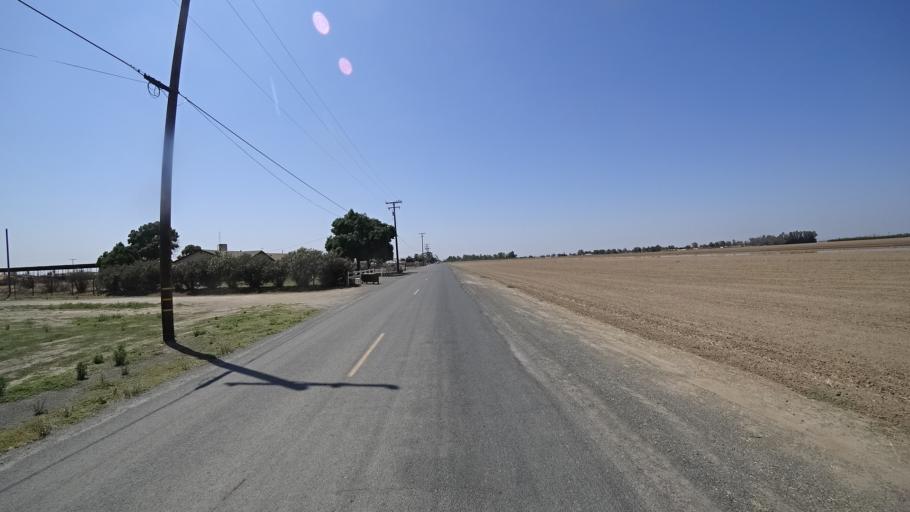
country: US
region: California
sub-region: Kings County
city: Home Garden
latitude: 36.3110
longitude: -119.6101
